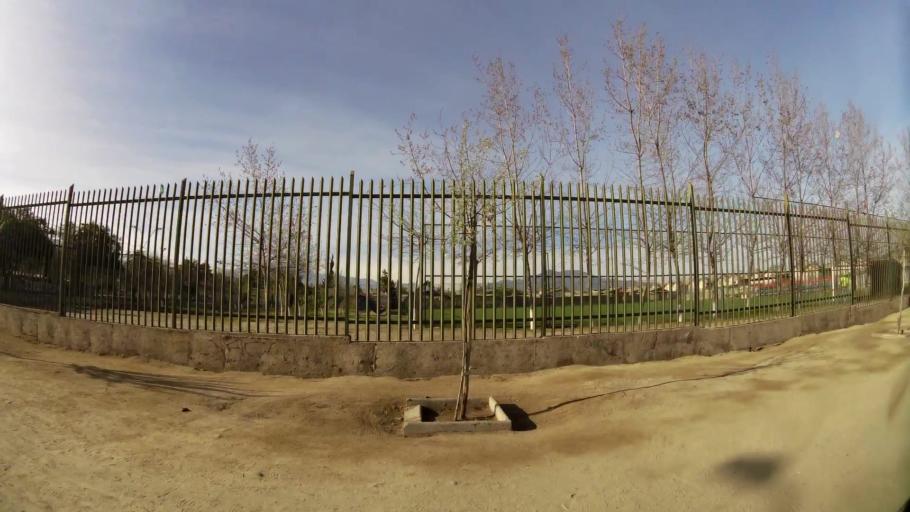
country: CL
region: Santiago Metropolitan
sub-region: Provincia de Cordillera
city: Puente Alto
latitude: -33.6120
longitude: -70.5920
